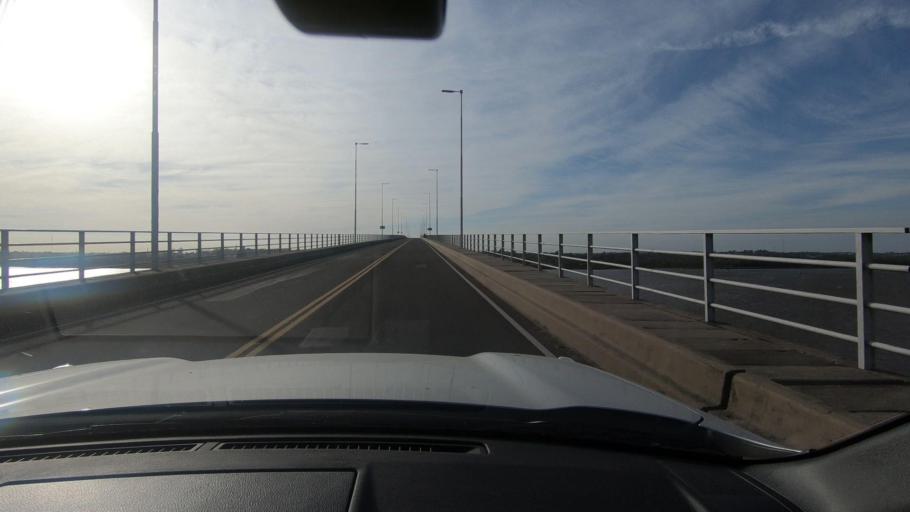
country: AR
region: Entre Rios
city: Colon
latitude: -32.2392
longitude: -58.1560
